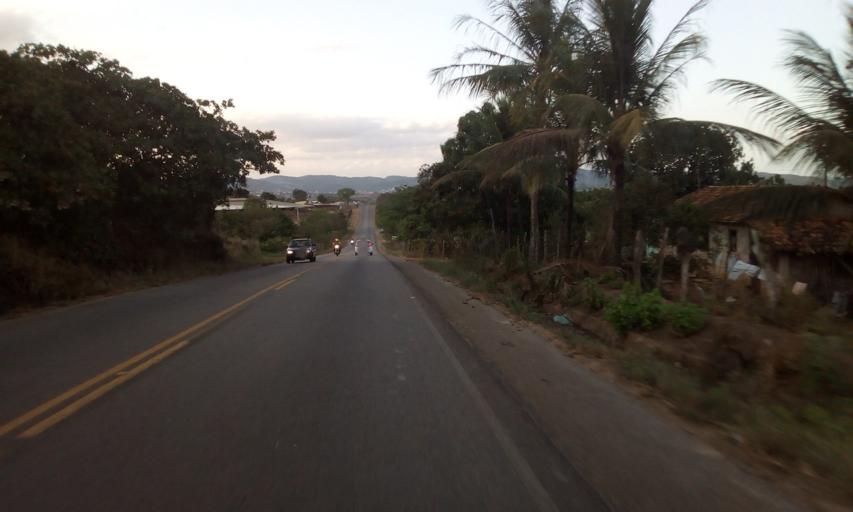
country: BR
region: Paraiba
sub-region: Guarabira
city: Guarabira
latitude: -6.8960
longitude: -35.4627
